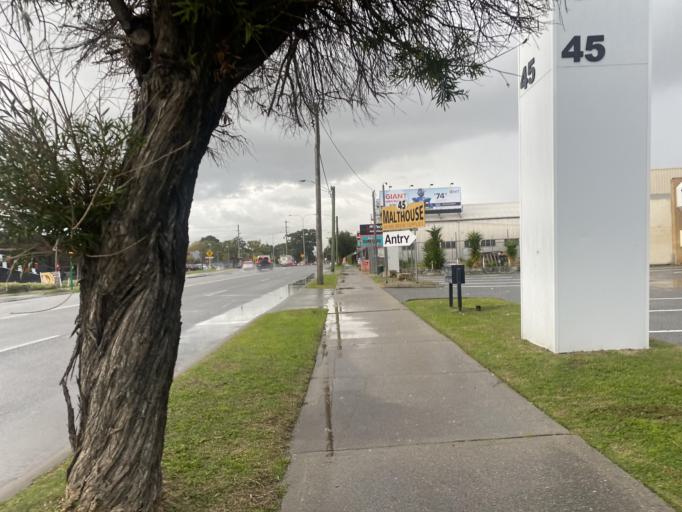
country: AU
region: Western Australia
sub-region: Canning
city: Bentley
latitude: -31.9941
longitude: 115.9193
